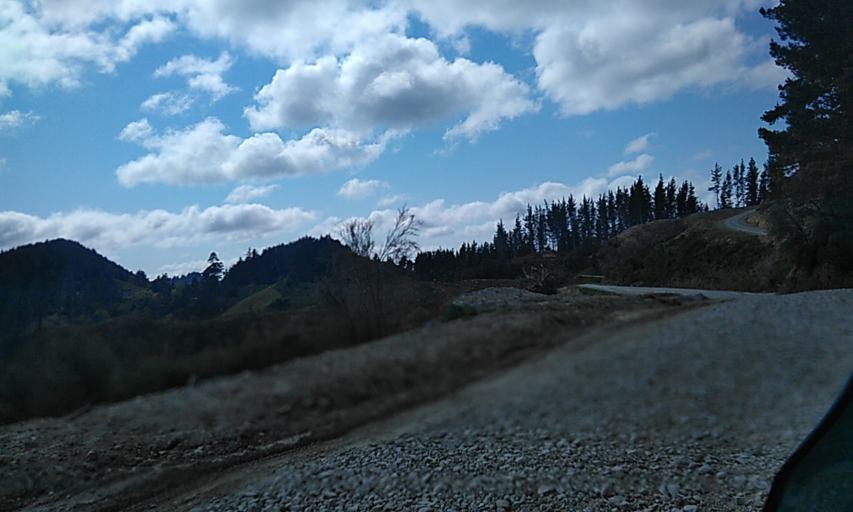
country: NZ
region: Gisborne
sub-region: Gisborne District
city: Gisborne
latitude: -38.3218
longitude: 178.0804
